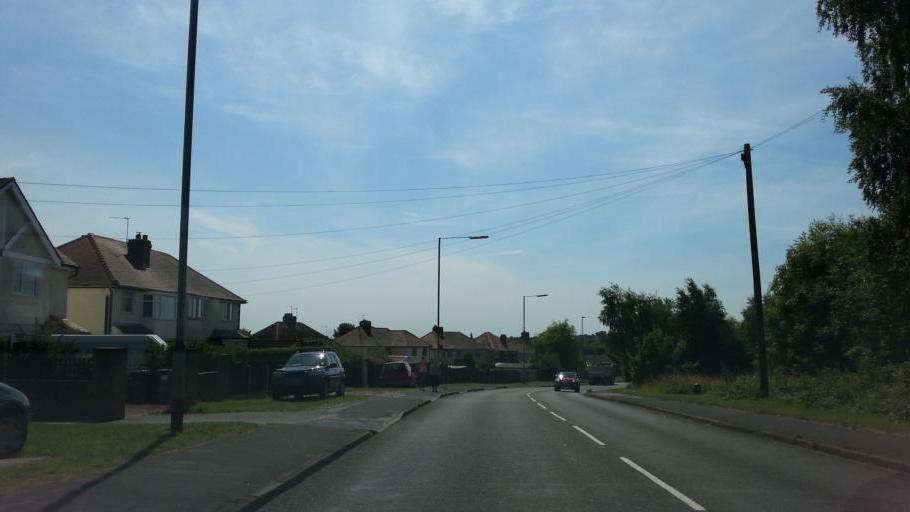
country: GB
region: England
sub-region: Staffordshire
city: Cannock
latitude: 52.7016
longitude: -2.0014
